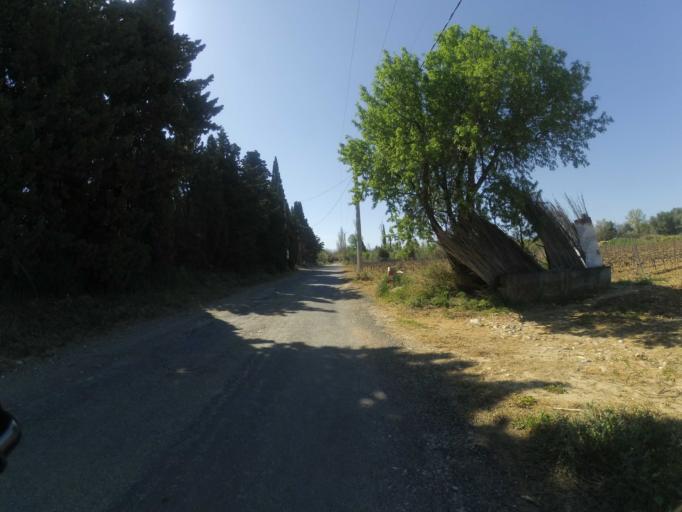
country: FR
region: Languedoc-Roussillon
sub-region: Departement des Pyrenees-Orientales
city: Pezilla-la-Riviere
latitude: 42.7055
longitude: 2.7738
